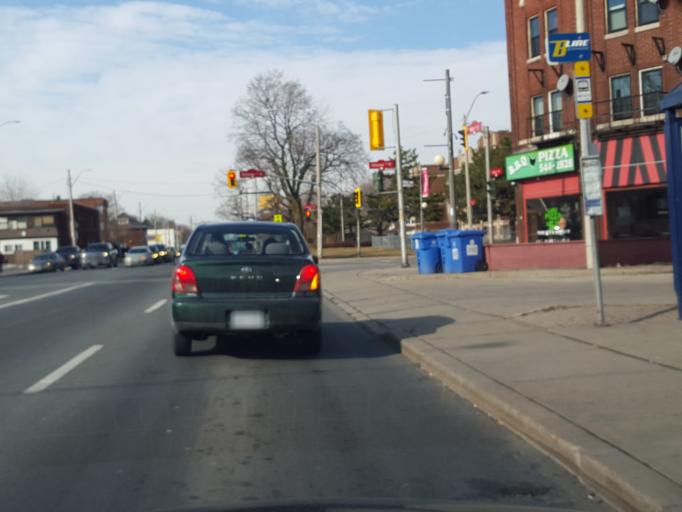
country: CA
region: Ontario
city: Hamilton
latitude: 43.2425
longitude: -79.8191
